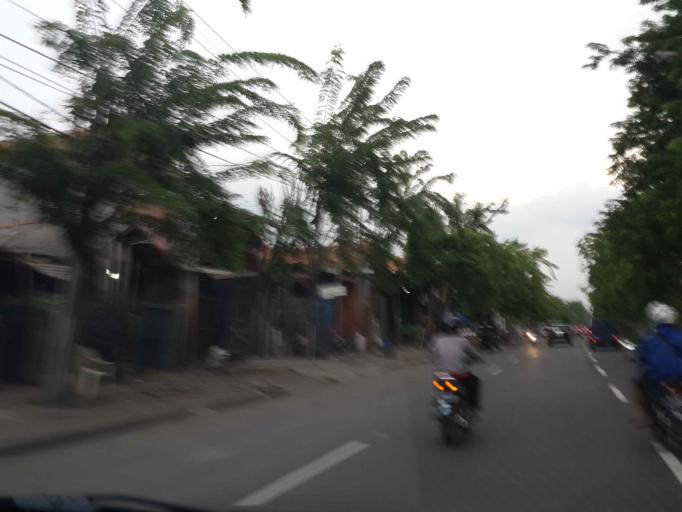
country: ID
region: East Java
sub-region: Kota Surabaya
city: Surabaya
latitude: -7.2491
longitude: 112.7209
